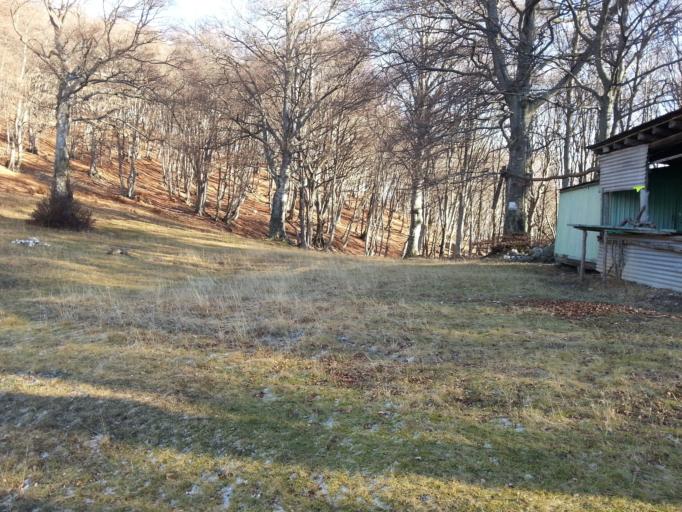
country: CH
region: Ticino
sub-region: Lugano District
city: Cadro
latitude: 46.0390
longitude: 9.0115
